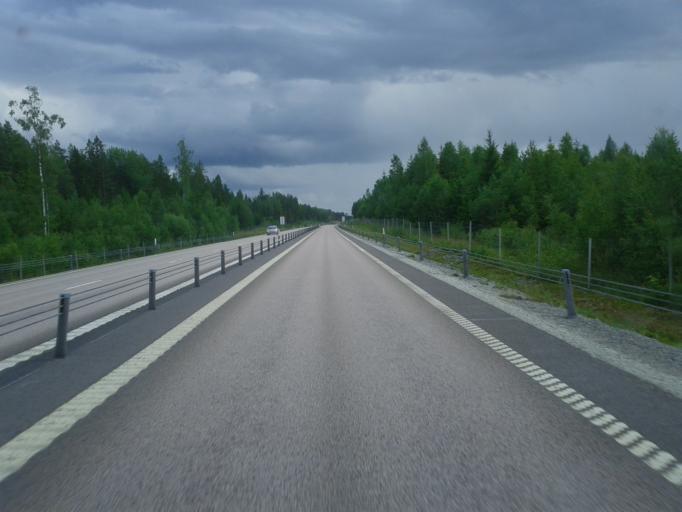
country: SE
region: Vaestmanland
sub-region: Sala Kommun
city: Sala
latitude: 59.9445
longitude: 16.5053
